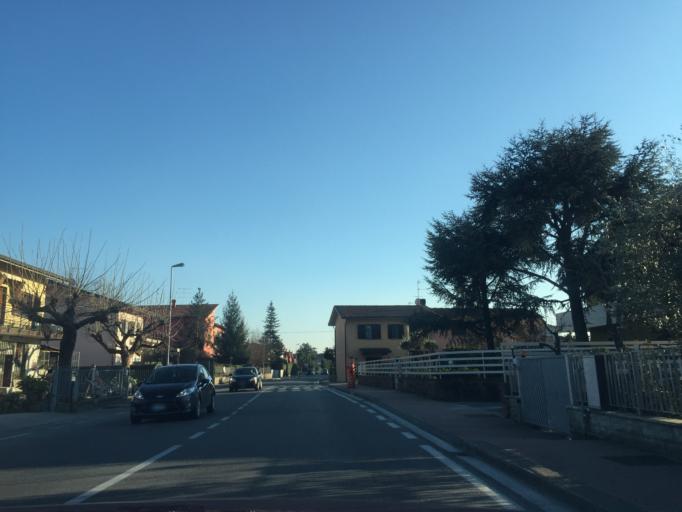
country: IT
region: Tuscany
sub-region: Provincia di Pistoia
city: Ponte Buggianese
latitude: 43.8490
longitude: 10.7462
